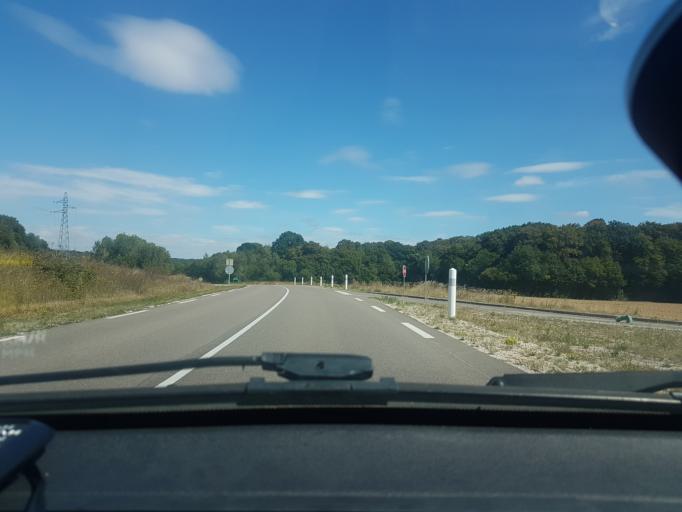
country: FR
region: Franche-Comte
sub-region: Departement de la Haute-Saone
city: Gray-la-Ville
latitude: 47.4051
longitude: 5.4913
